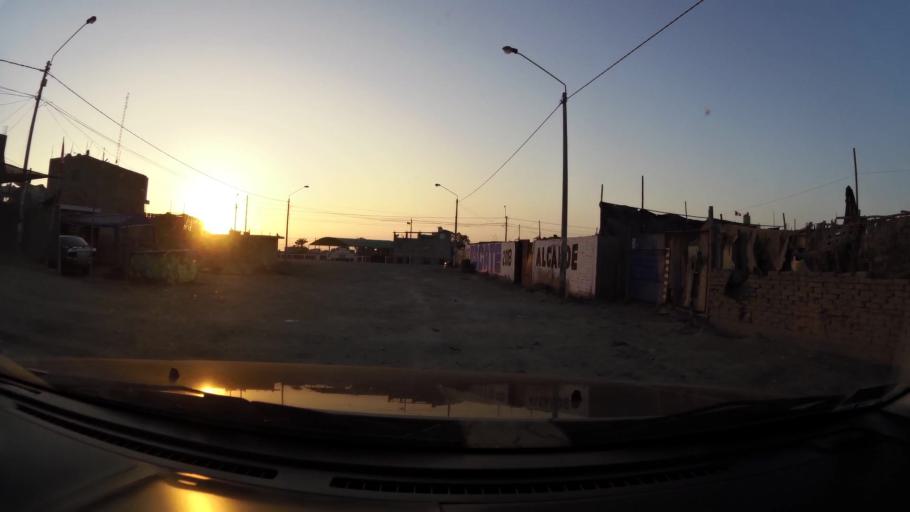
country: PE
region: Ica
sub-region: Provincia de Pisco
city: San Clemente
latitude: -13.6730
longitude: -76.1563
